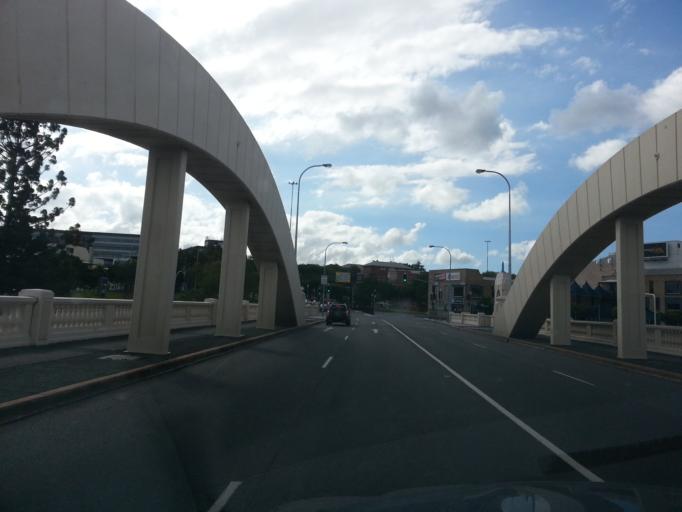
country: AU
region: Queensland
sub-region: Brisbane
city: Spring Hill
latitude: -27.4681
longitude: 153.0154
